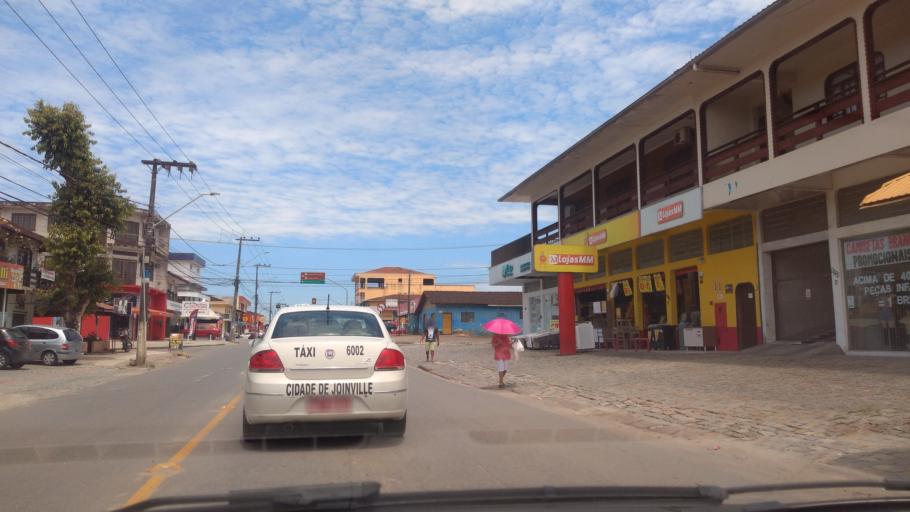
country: BR
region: Santa Catarina
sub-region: Joinville
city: Joinville
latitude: -26.3210
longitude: -48.8163
